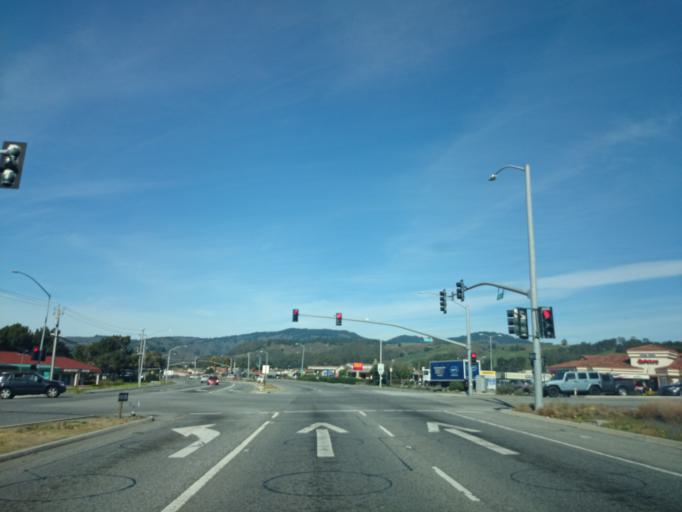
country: US
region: California
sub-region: San Mateo County
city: Half Moon Bay
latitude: 37.4677
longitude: -122.4335
